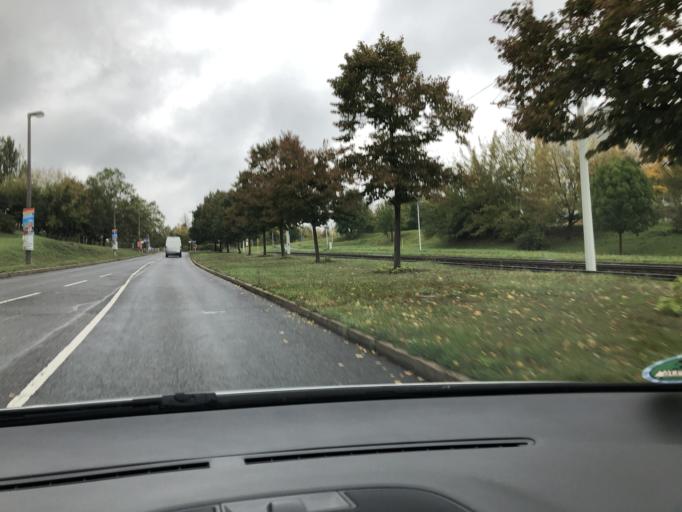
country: DE
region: Thuringia
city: Gera
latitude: 50.9017
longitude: 12.0938
